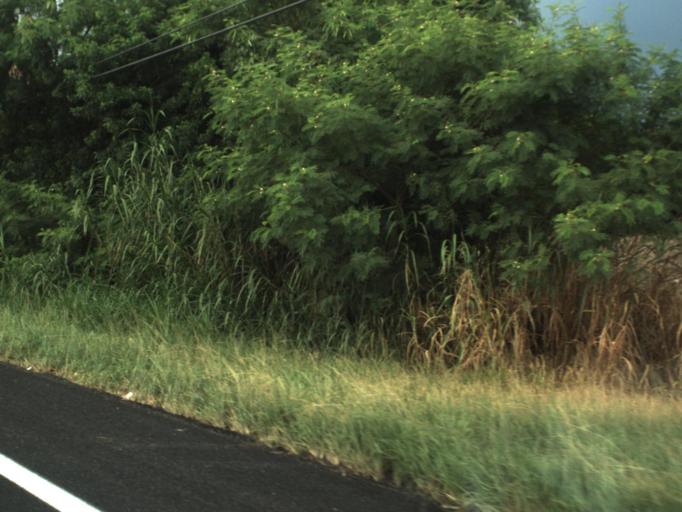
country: US
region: Florida
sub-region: Miami-Dade County
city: Homestead
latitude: 25.5060
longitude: -80.4777
